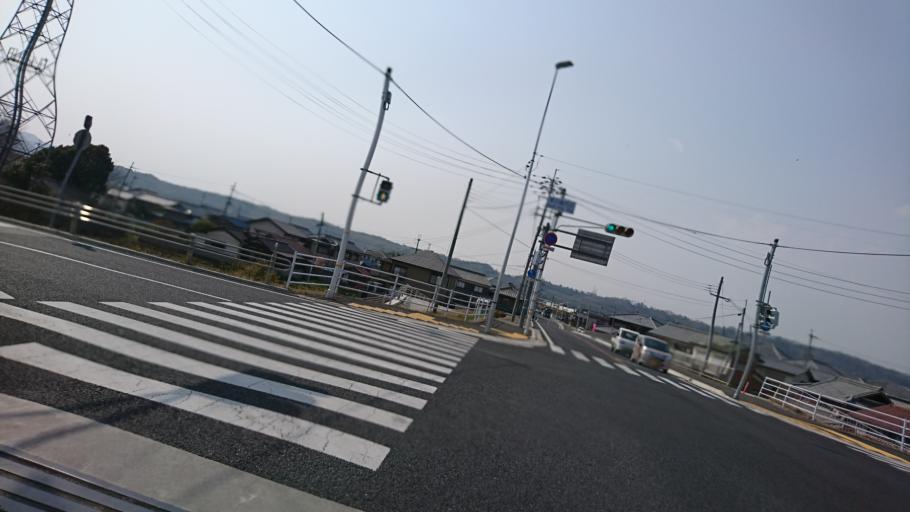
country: JP
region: Hyogo
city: Ono
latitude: 34.8626
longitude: 134.9155
